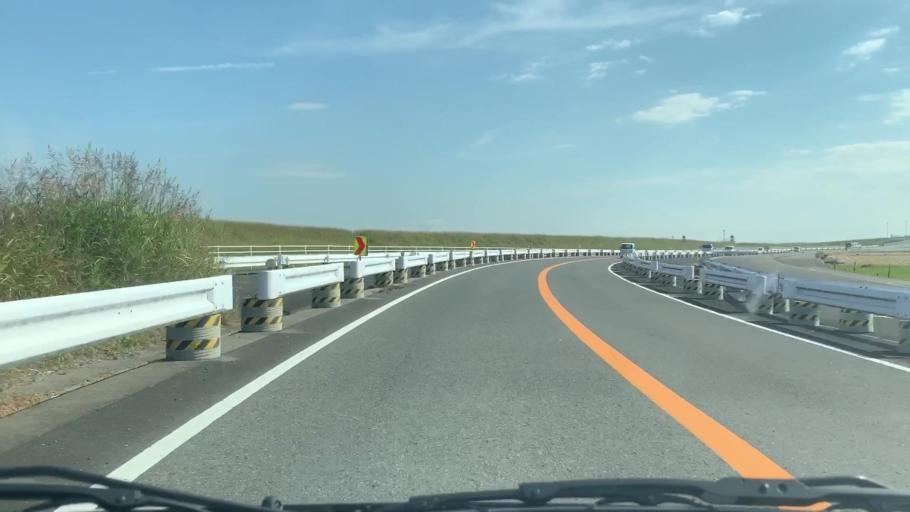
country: JP
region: Saga Prefecture
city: Saga-shi
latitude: 33.2246
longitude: 130.1881
